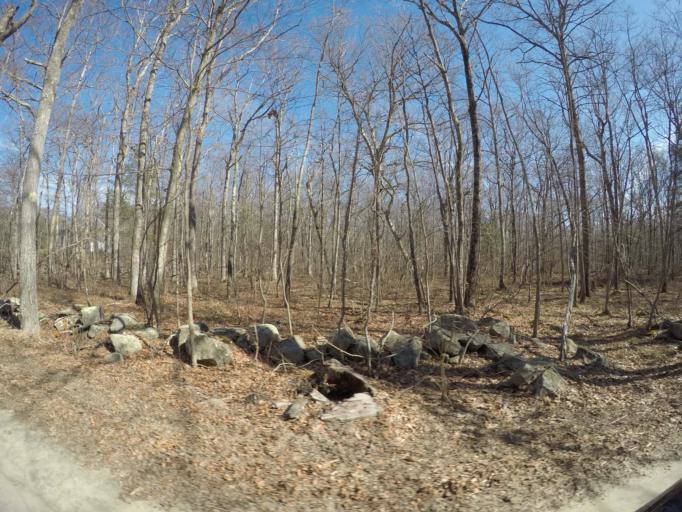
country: US
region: Massachusetts
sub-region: Norfolk County
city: Sharon
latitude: 42.0771
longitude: -71.1489
